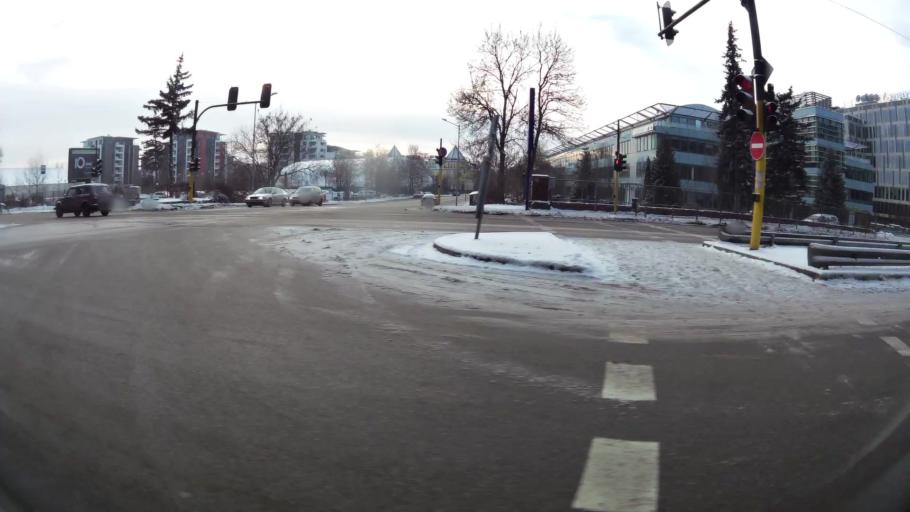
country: BG
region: Sofia-Capital
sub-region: Stolichna Obshtina
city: Sofia
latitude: 42.6676
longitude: 23.3263
